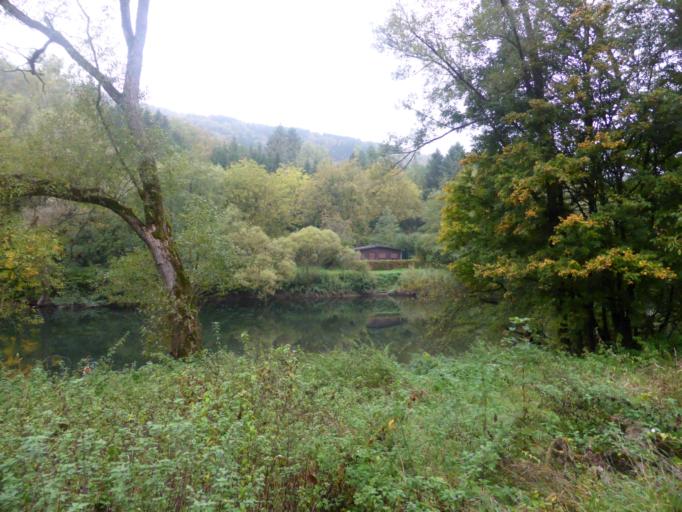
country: DE
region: Rheinland-Pfalz
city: Oberbillig
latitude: 49.7362
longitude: 6.5023
